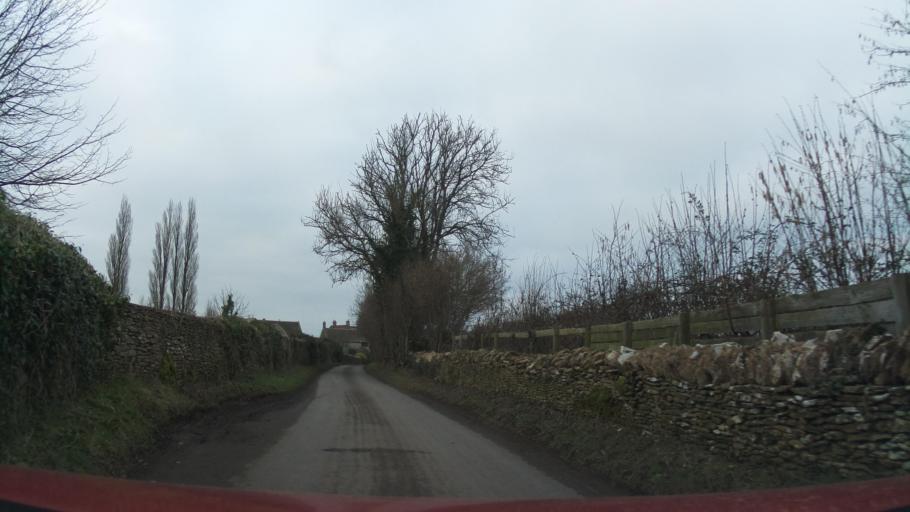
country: GB
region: England
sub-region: Wiltshire
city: Nettleton
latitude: 51.4913
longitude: -2.2781
